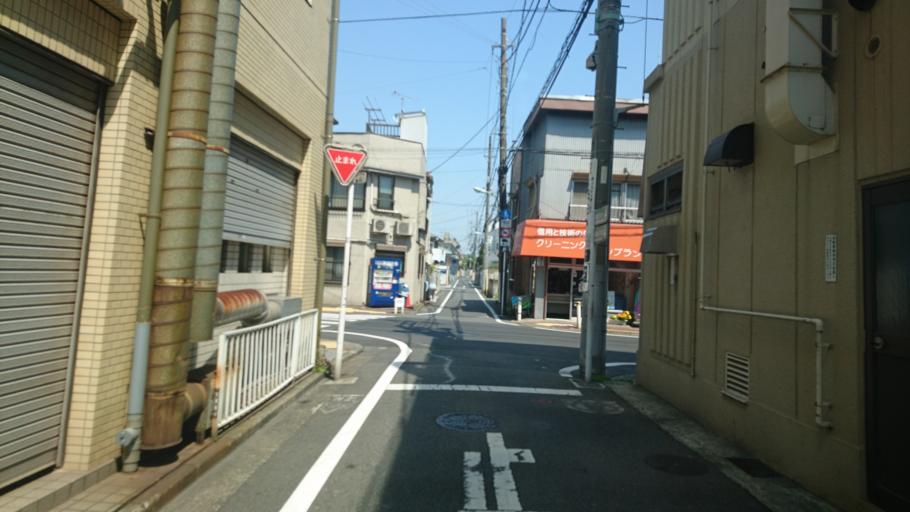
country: JP
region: Kanagawa
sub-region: Kawasaki-shi
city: Kawasaki
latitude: 35.5680
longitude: 139.7406
